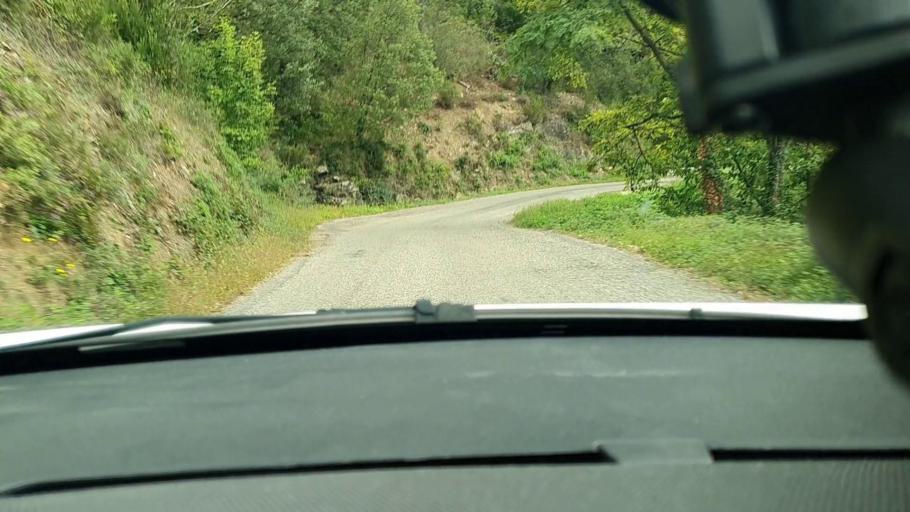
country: FR
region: Languedoc-Roussillon
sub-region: Departement du Gard
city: Branoux-les-Taillades
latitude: 44.2595
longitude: 3.9780
